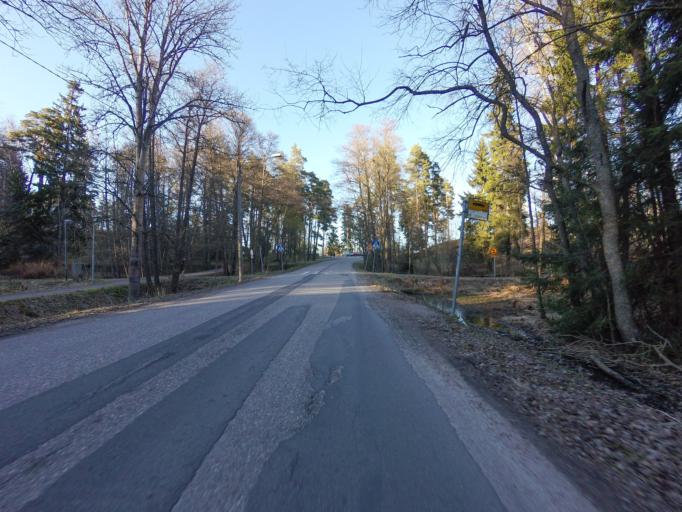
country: FI
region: Uusimaa
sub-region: Helsinki
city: Helsinki
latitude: 60.1767
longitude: 25.0267
